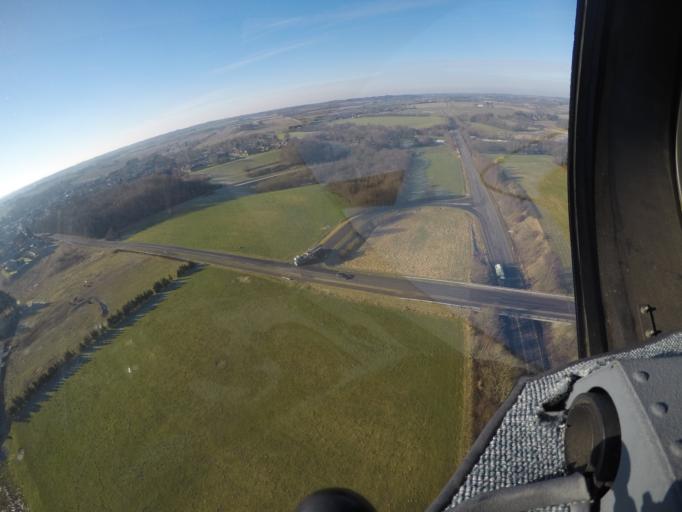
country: DK
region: South Denmark
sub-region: Kolding Kommune
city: Kolding
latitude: 55.5713
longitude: 9.4099
